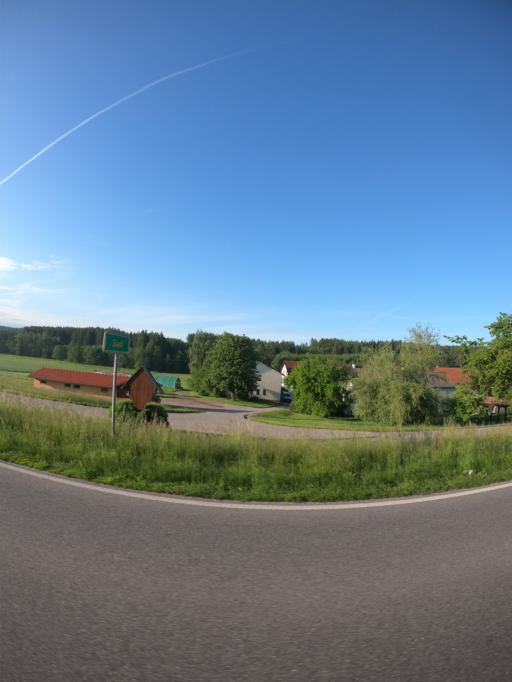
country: DE
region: Bavaria
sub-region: Upper Bavaria
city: Taufkirchen
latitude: 48.3424
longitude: 12.1051
